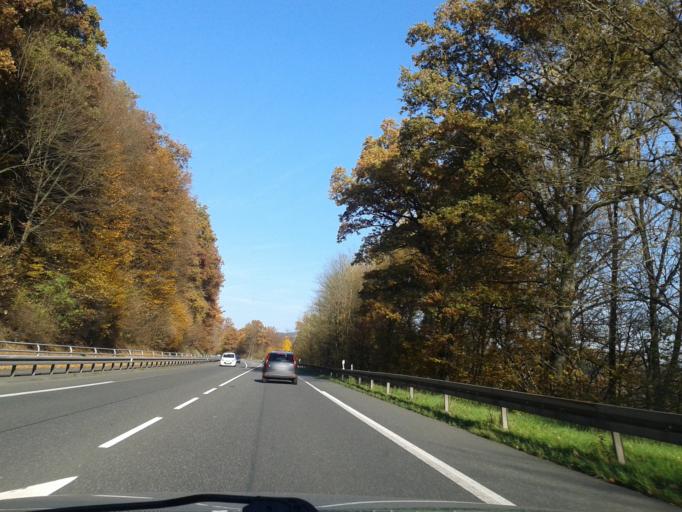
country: DE
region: Hesse
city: Dillenburg
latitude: 50.7979
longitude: 8.3336
